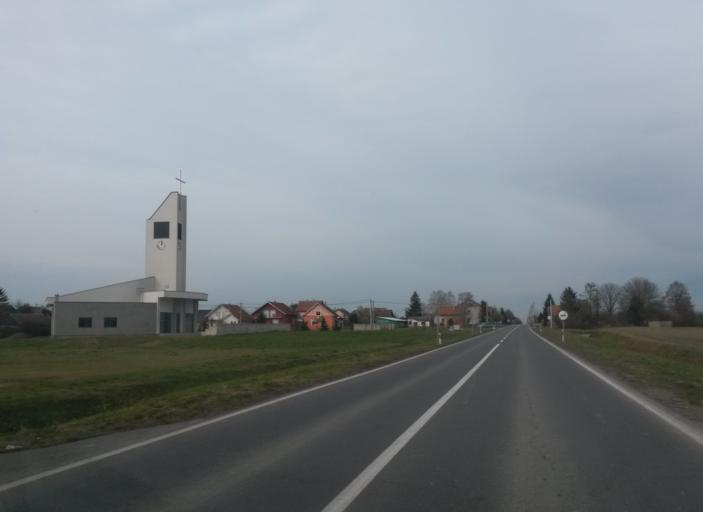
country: HR
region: Osjecko-Baranjska
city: Antunovac
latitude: 45.4891
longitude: 18.6758
